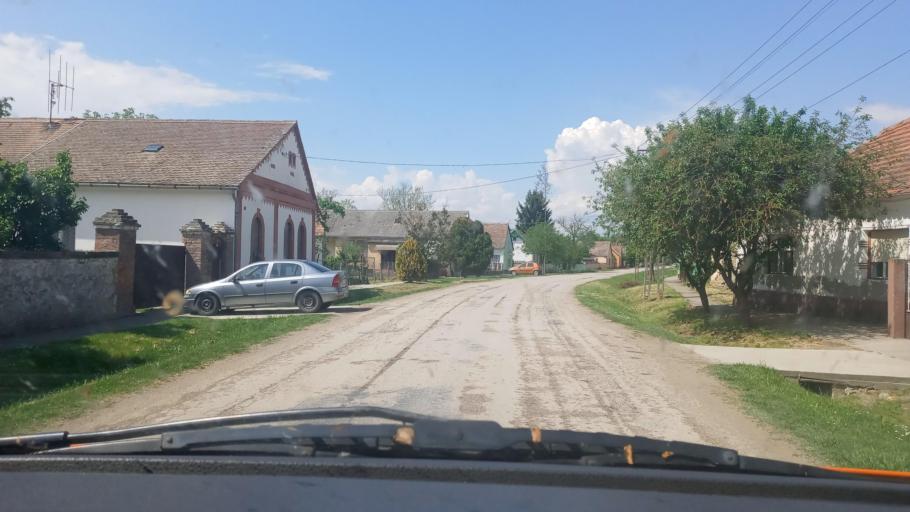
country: HU
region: Baranya
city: Beremend
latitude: 45.7907
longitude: 18.3508
